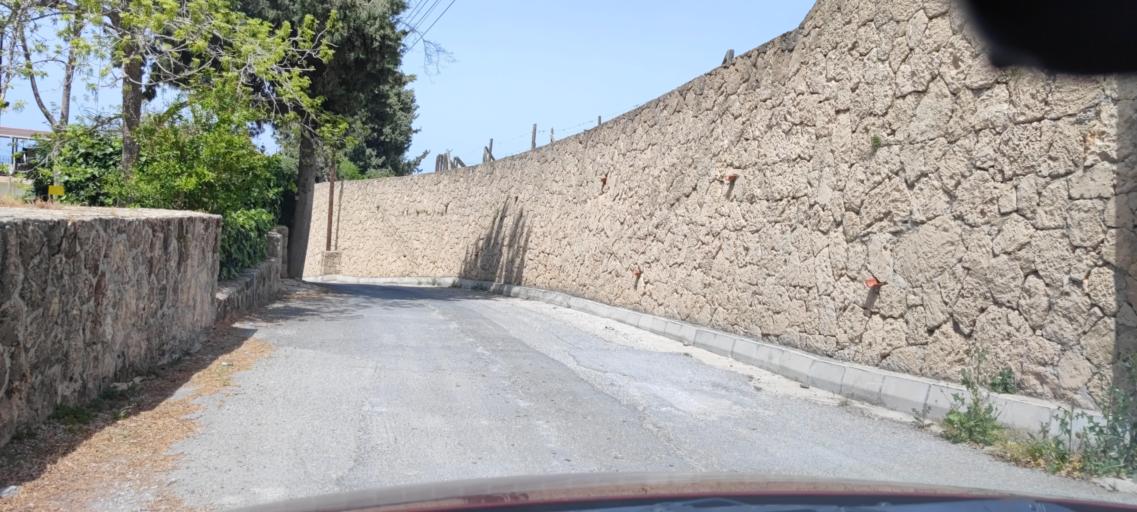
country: CY
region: Keryneia
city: Kyrenia
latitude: 35.3064
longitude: 33.3576
